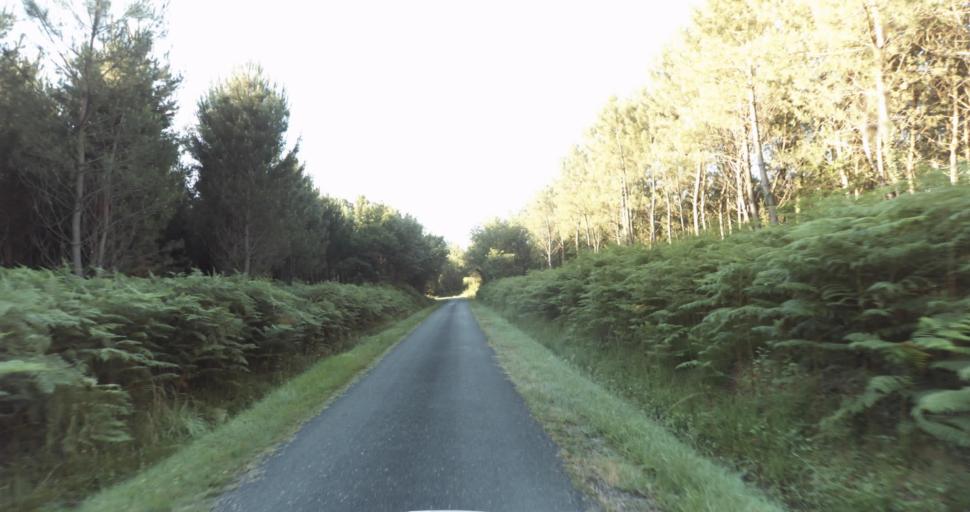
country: FR
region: Aquitaine
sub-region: Departement de la Gironde
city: Bazas
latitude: 44.4133
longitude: -0.2336
